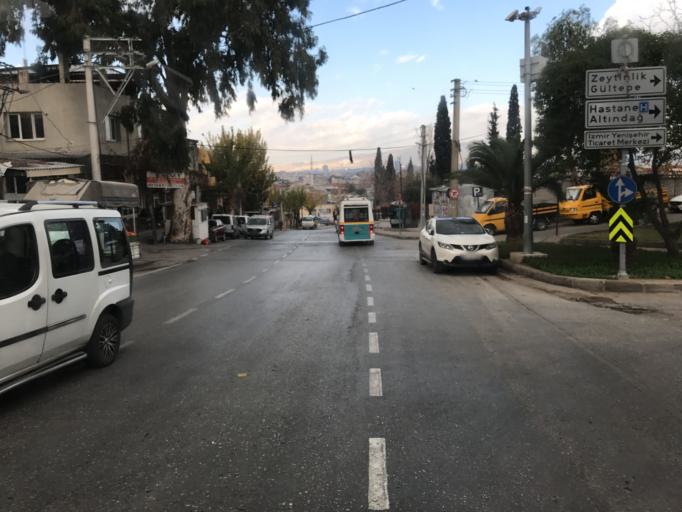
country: TR
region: Izmir
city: Buca
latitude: 38.4135
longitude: 27.1612
